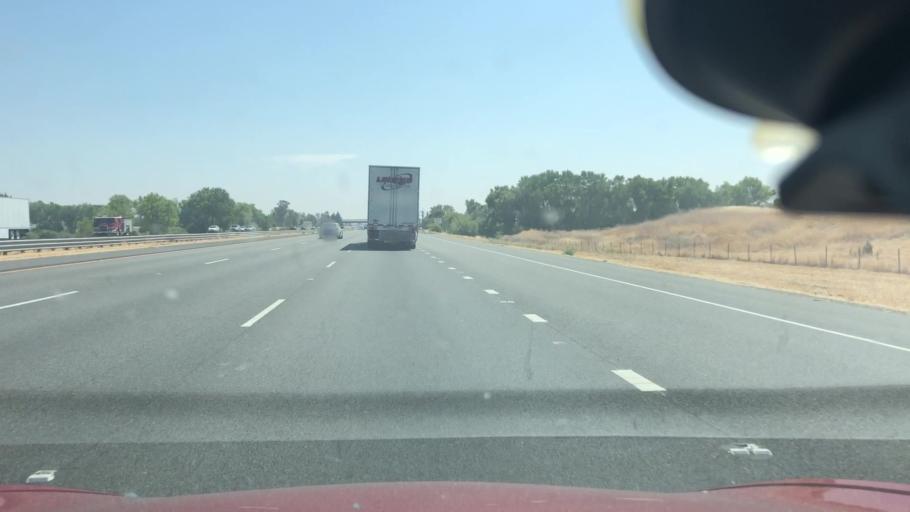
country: US
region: California
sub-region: Sacramento County
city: Laguna
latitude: 38.4346
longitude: -121.4893
